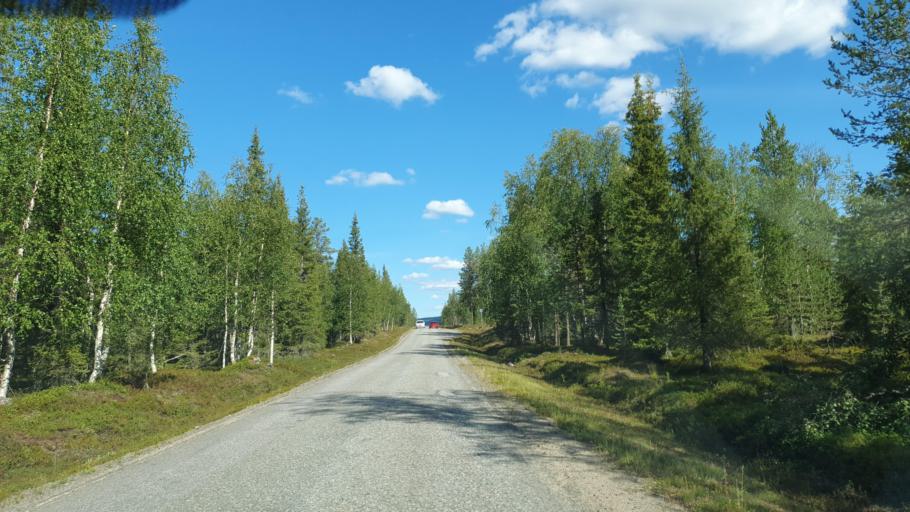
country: FI
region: Lapland
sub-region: Tunturi-Lappi
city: Muonio
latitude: 67.6942
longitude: 24.1117
